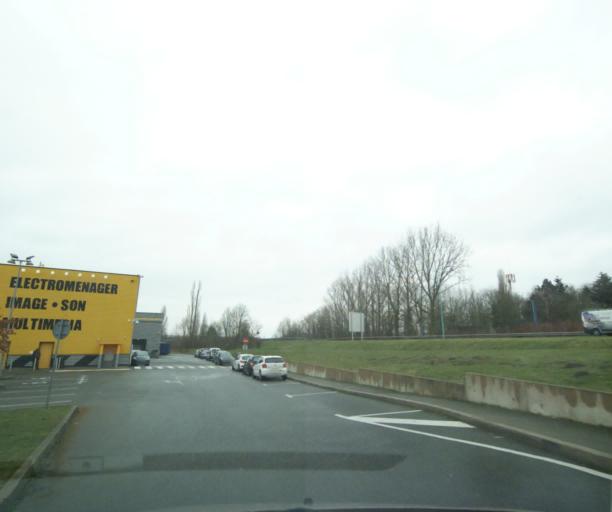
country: FR
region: Nord-Pas-de-Calais
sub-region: Departement du Nord
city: Herin
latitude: 50.3380
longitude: 3.4632
